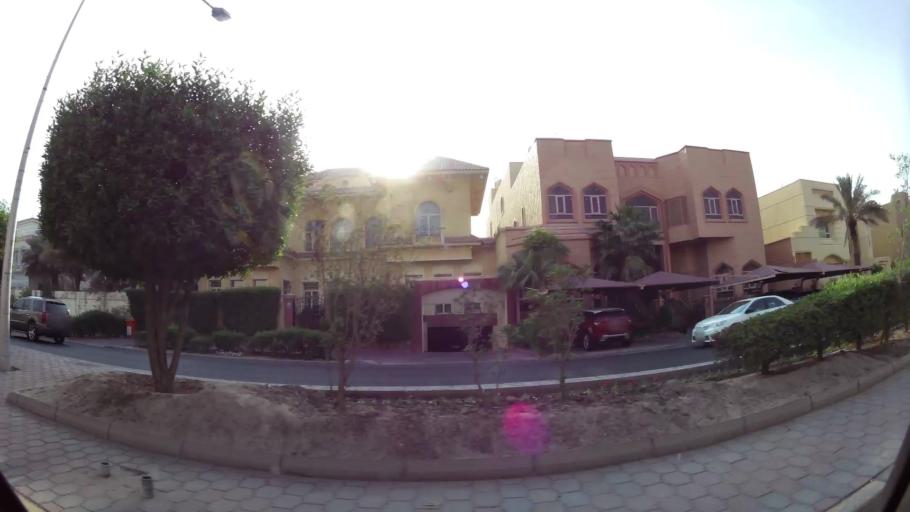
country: KW
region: Muhafazat Hawalli
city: Hawalli
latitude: 29.3095
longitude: 48.0084
